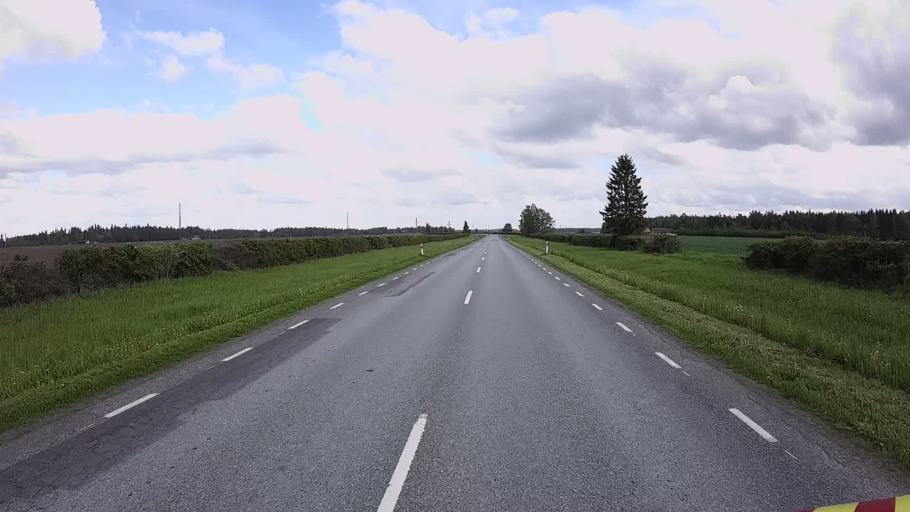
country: EE
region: Laeaene-Virumaa
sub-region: Vinni vald
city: Vinni
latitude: 59.2182
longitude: 26.5369
